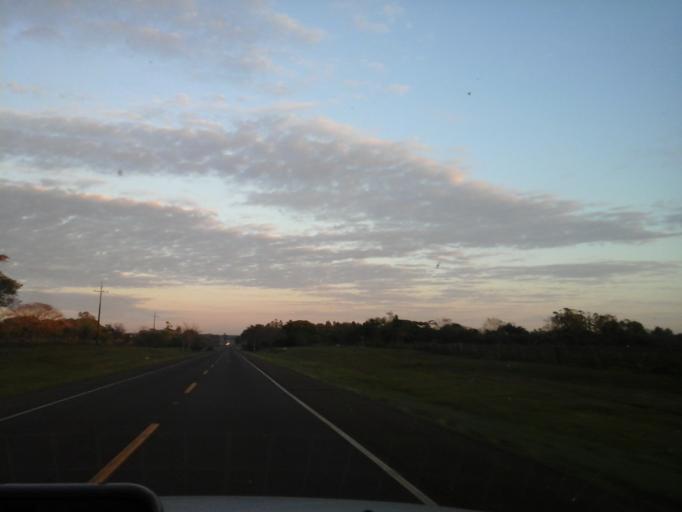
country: PY
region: Itapua
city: General Delgado
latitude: -27.0749
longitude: -56.5860
